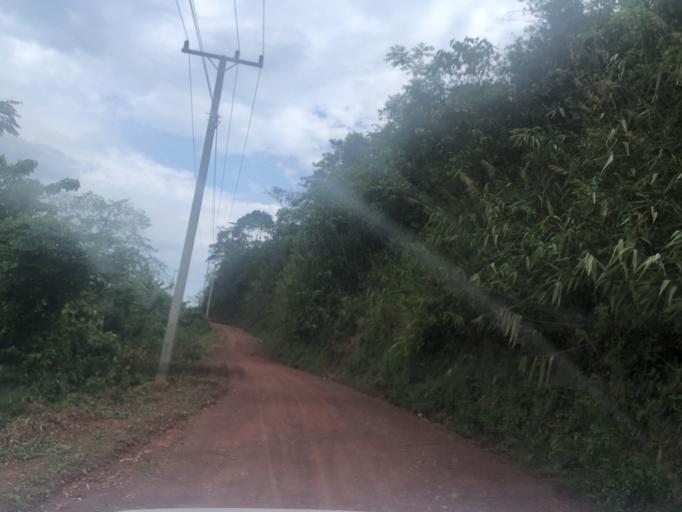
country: LA
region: Oudomxai
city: Muang La
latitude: 21.2536
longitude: 102.0049
